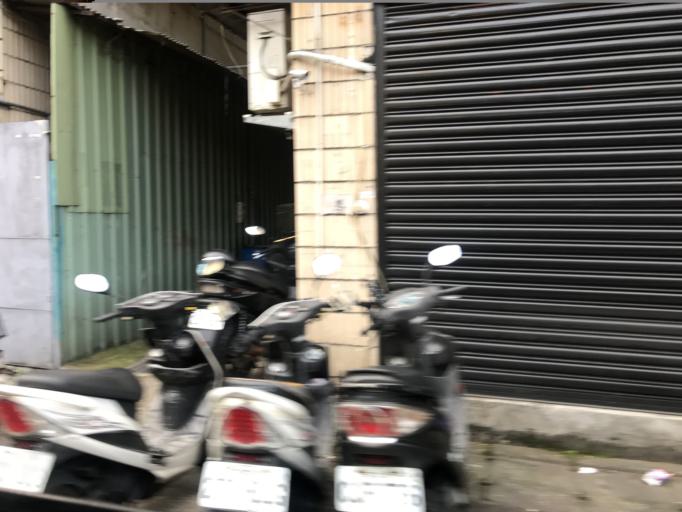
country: TW
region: Taipei
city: Taipei
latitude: 25.0831
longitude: 121.4867
